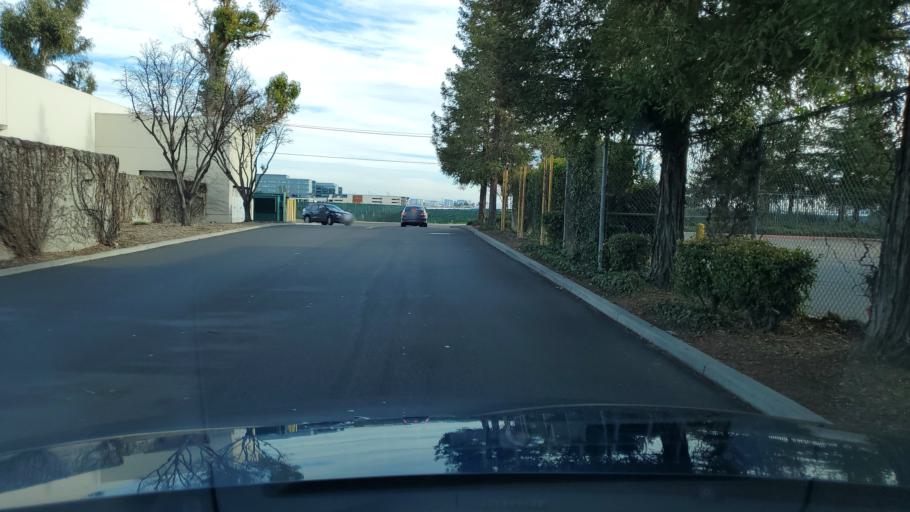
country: US
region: California
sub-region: Santa Clara County
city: Santa Clara
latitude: 37.3561
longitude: -121.9364
